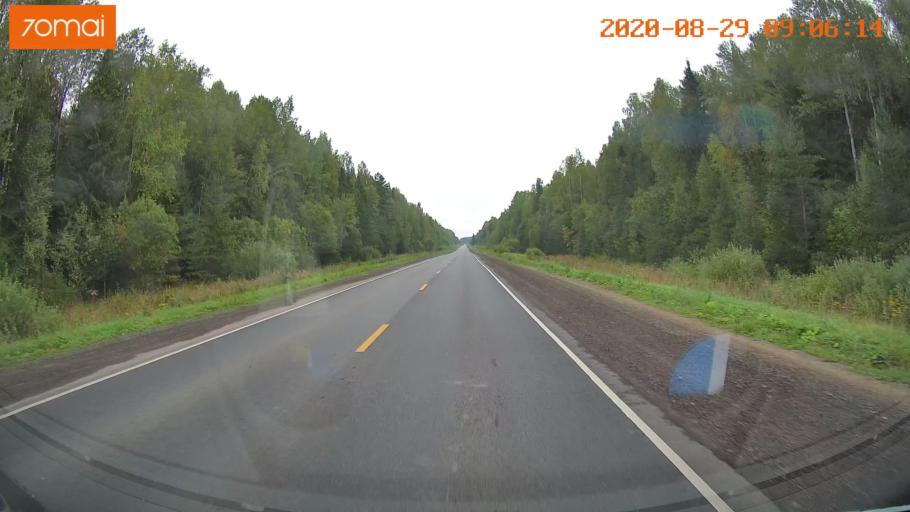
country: RU
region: Ivanovo
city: Navoloki
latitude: 57.3679
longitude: 42.0138
